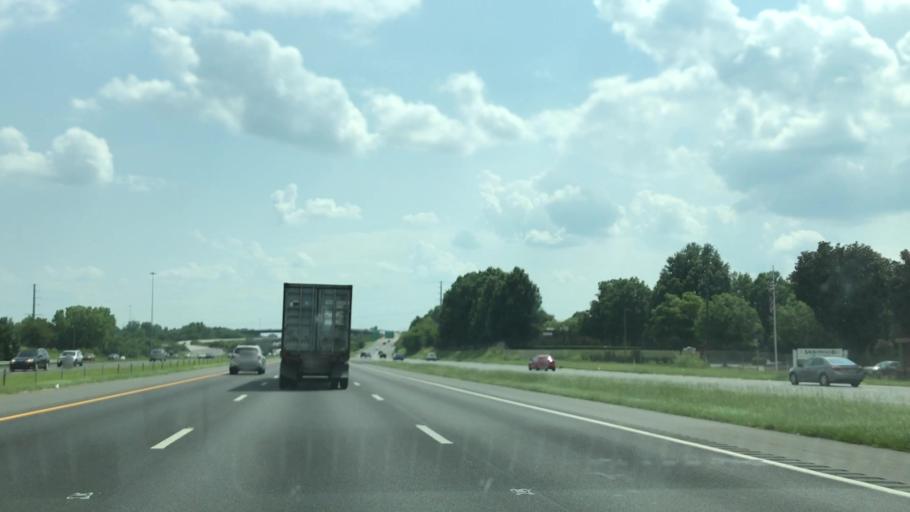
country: US
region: North Carolina
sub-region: Mecklenburg County
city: Pineville
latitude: 35.1324
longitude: -80.9129
